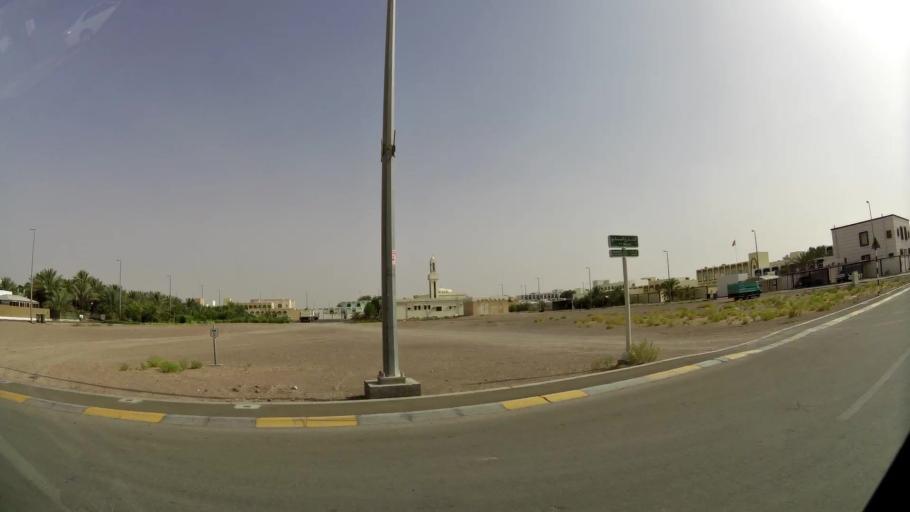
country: AE
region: Abu Dhabi
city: Al Ain
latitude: 24.2068
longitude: 55.5762
